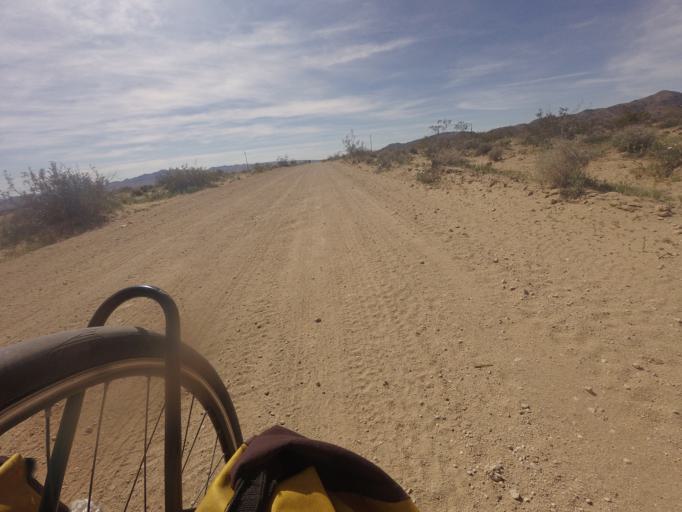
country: US
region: California
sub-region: San Bernardino County
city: Searles Valley
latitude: 35.5714
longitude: -117.4412
